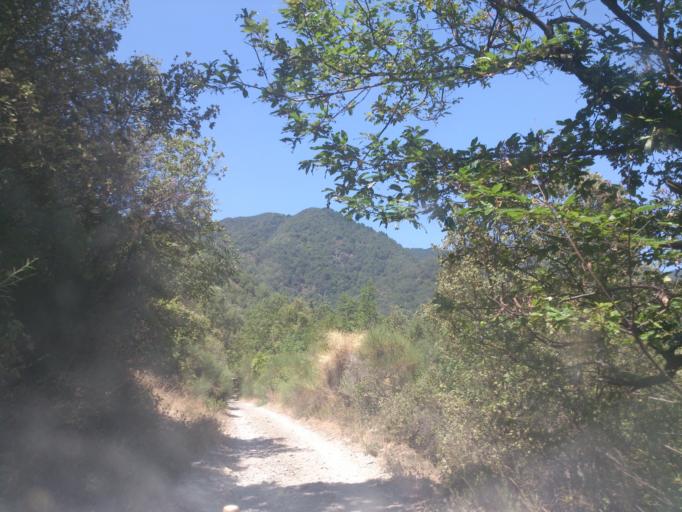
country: IT
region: Calabria
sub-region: Provincia di Reggio Calabria
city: Bivongi
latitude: 38.4893
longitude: 16.4127
